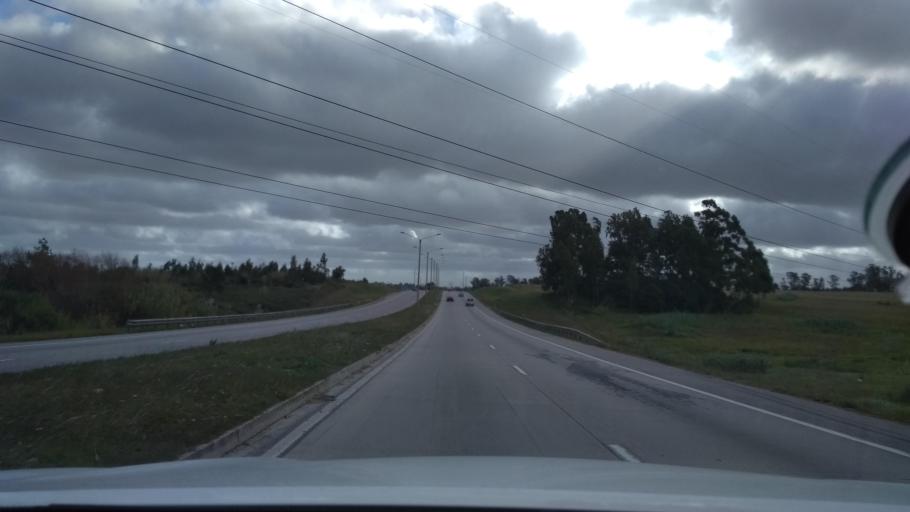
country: UY
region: Canelones
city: Toledo
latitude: -34.7911
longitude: -56.1020
